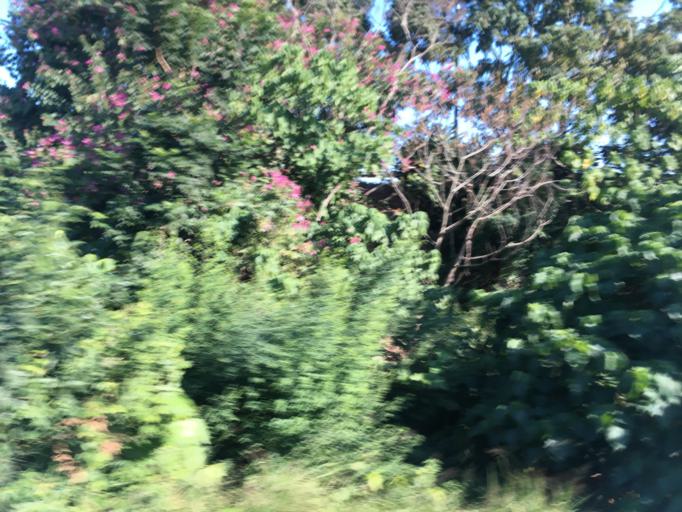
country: TW
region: Taiwan
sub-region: Chiayi
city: Jiayi Shi
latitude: 23.4500
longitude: 120.4839
